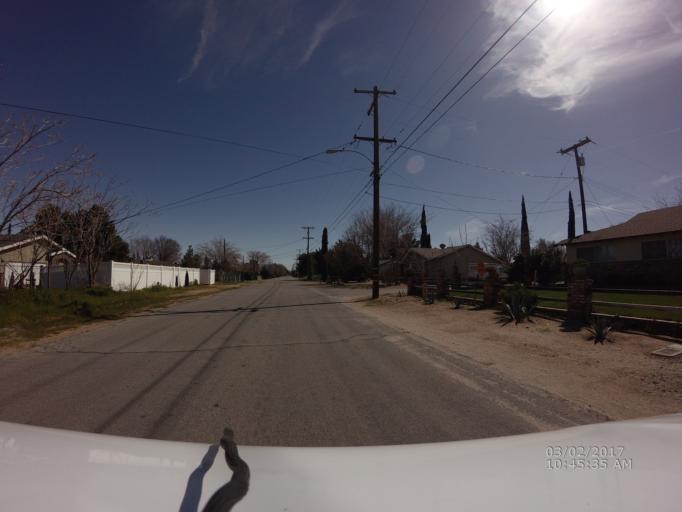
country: US
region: California
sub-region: Los Angeles County
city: Quartz Hill
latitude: 34.6416
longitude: -118.2253
